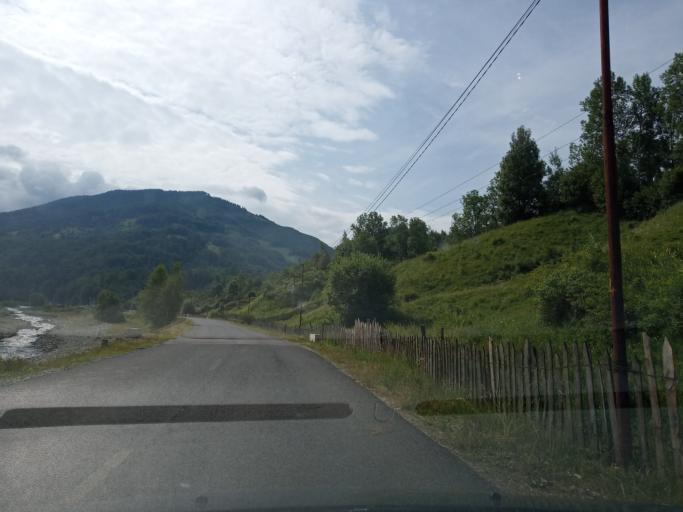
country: RO
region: Hunedoara
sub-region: Oras Petrila
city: Petrila
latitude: 45.4198
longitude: 23.4267
